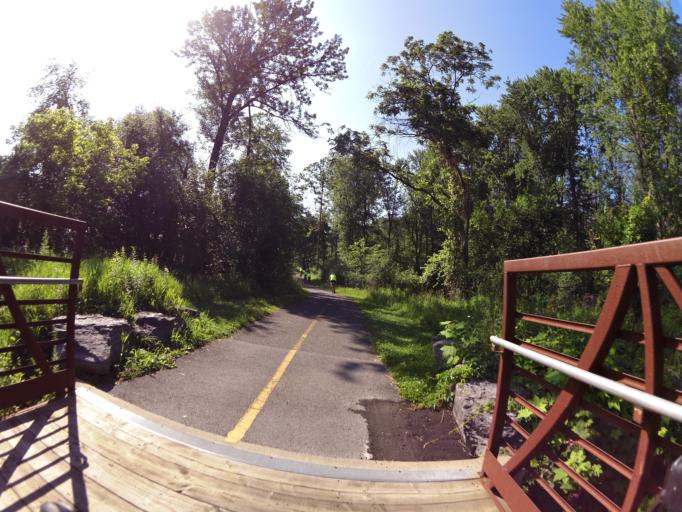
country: CA
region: Quebec
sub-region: Outaouais
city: Gatineau
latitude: 45.4599
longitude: -75.7239
